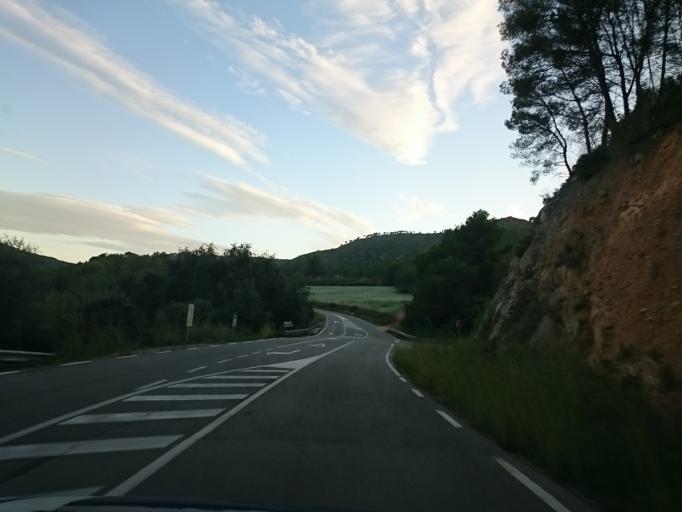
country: ES
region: Catalonia
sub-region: Provincia de Barcelona
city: Sant Pere de Ribes
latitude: 41.2901
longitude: 1.7766
